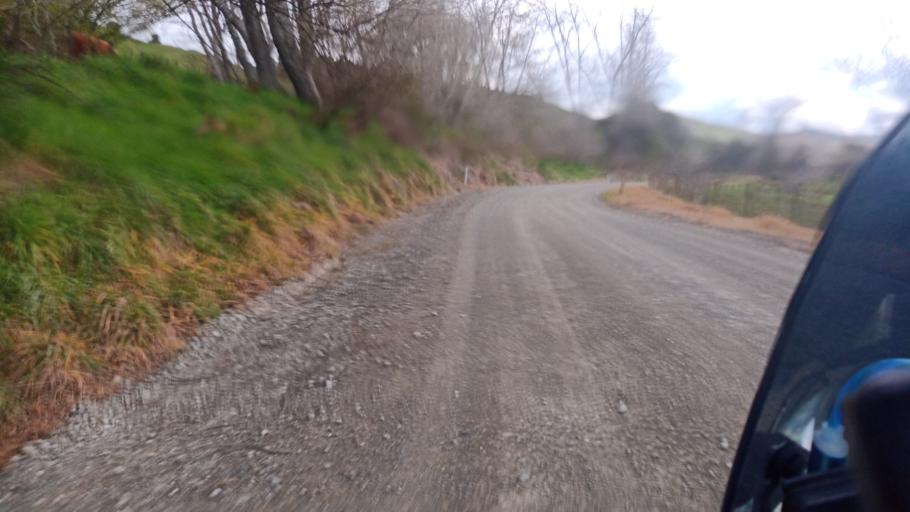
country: NZ
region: Gisborne
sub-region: Gisborne District
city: Gisborne
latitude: -38.2029
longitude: 178.2440
